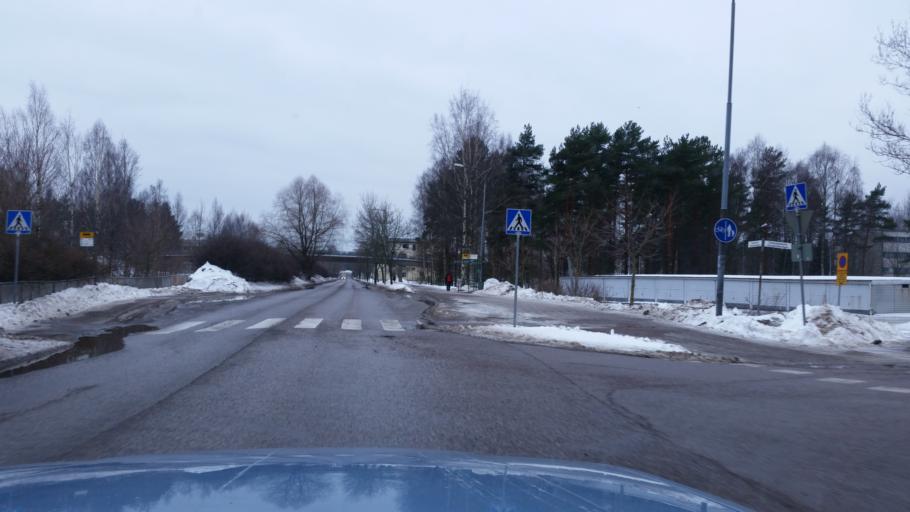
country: FI
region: Uusimaa
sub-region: Helsinki
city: Vantaa
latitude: 60.2339
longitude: 25.0784
